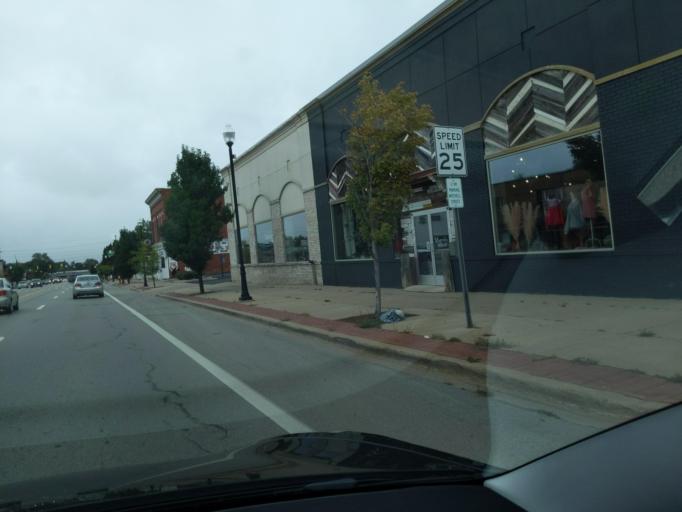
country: US
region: Michigan
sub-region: Wexford County
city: Cadillac
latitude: 44.2532
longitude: -85.4017
